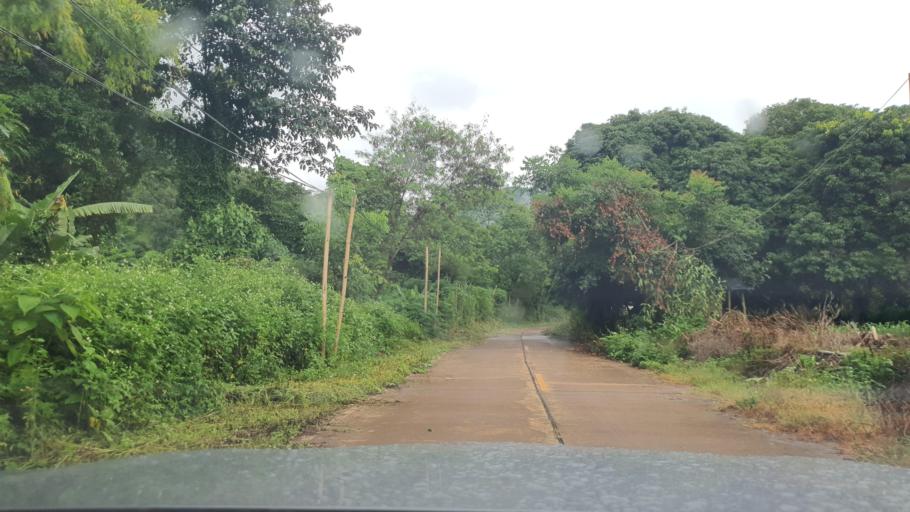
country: TH
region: Chiang Mai
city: Samoeng
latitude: 18.8294
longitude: 98.7703
